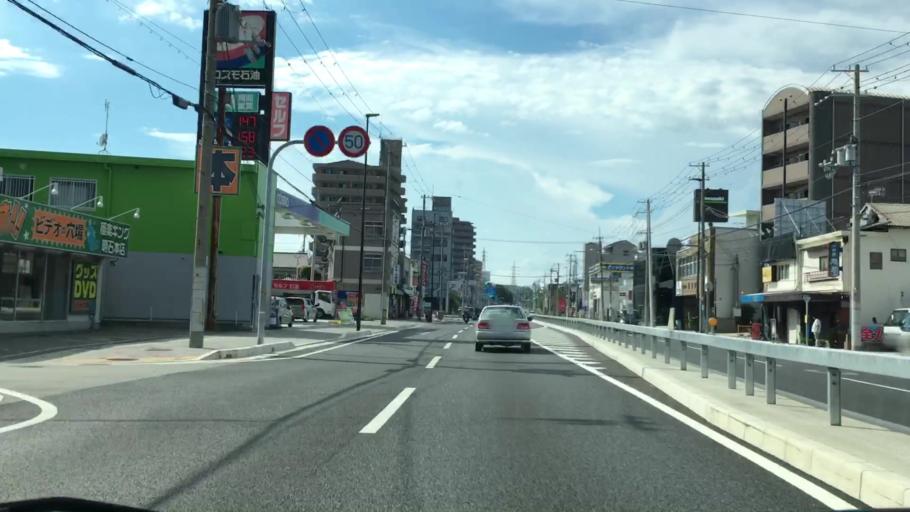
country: JP
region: Hyogo
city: Akashi
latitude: 34.6511
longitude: 134.9799
